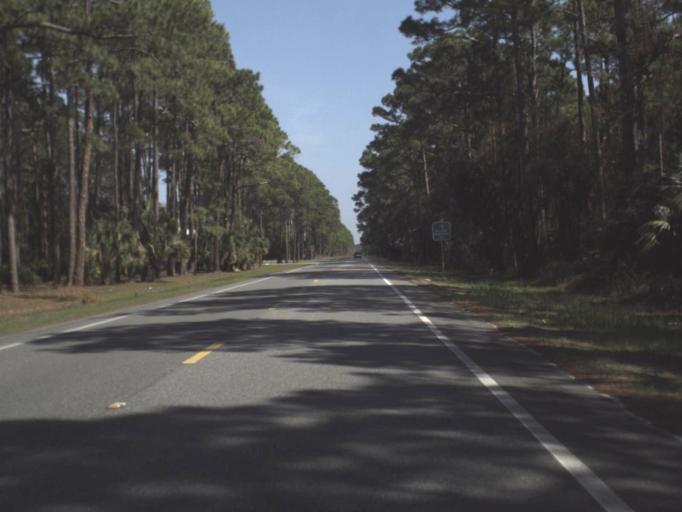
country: US
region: Florida
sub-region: Franklin County
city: Apalachicola
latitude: 29.7163
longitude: -85.0415
